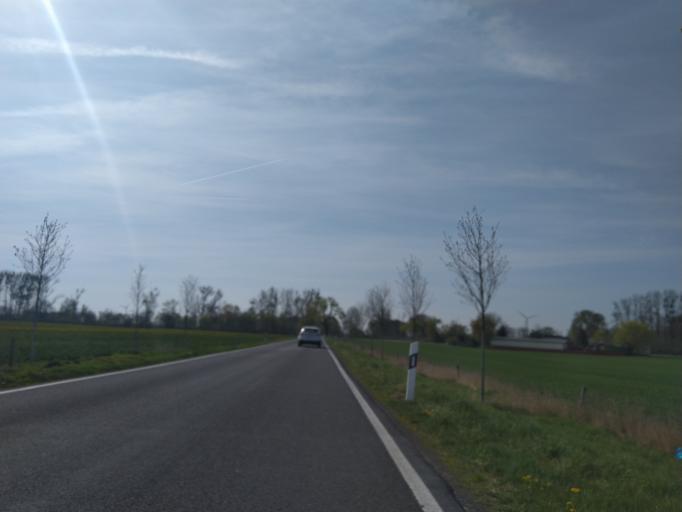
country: DE
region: Brandenburg
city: Bliesdorf
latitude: 52.7264
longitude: 14.1704
